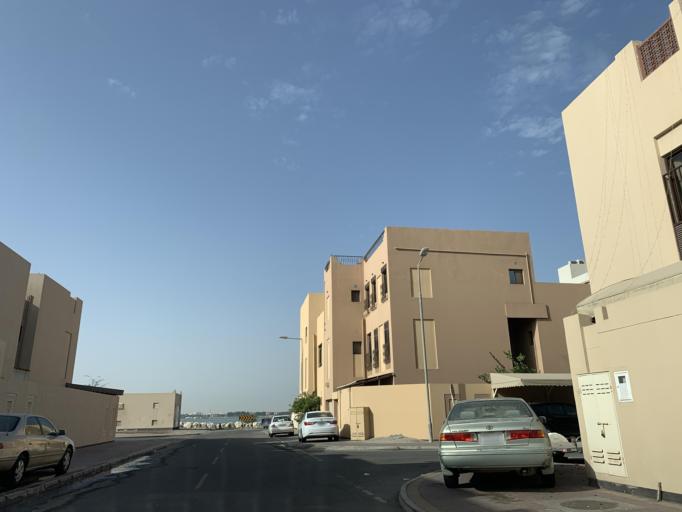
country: BH
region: Manama
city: Manama
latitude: 26.1789
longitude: 50.5898
